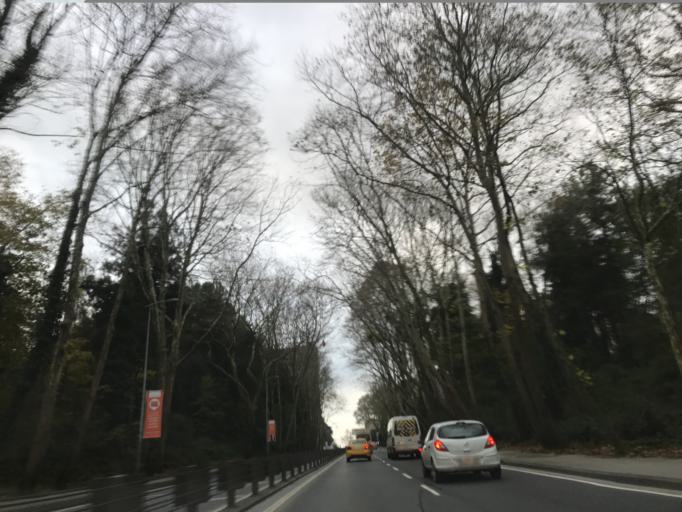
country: TR
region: Istanbul
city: Arikoey
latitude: 41.1452
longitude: 29.0281
